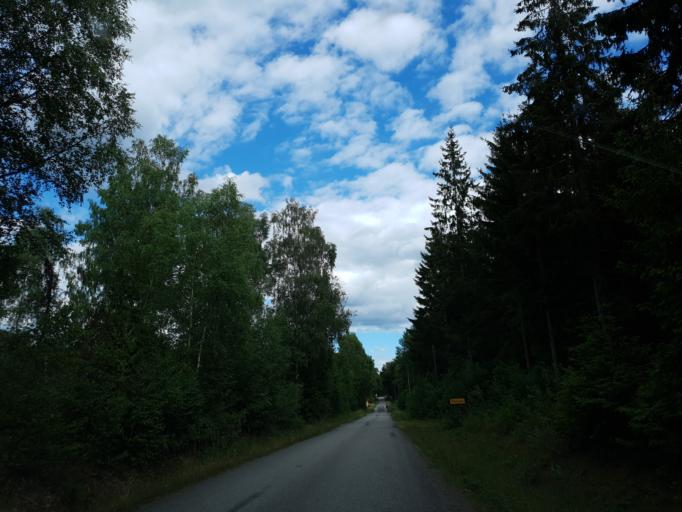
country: SE
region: Kalmar
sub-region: Emmaboda Kommun
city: Emmaboda
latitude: 56.6233
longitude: 15.6628
